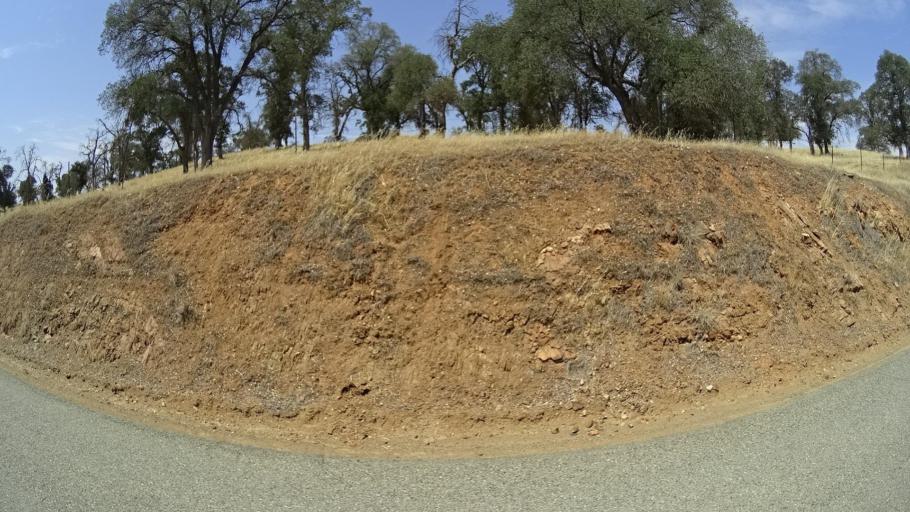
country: US
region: California
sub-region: Merced County
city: Planada
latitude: 37.5201
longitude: -120.2285
